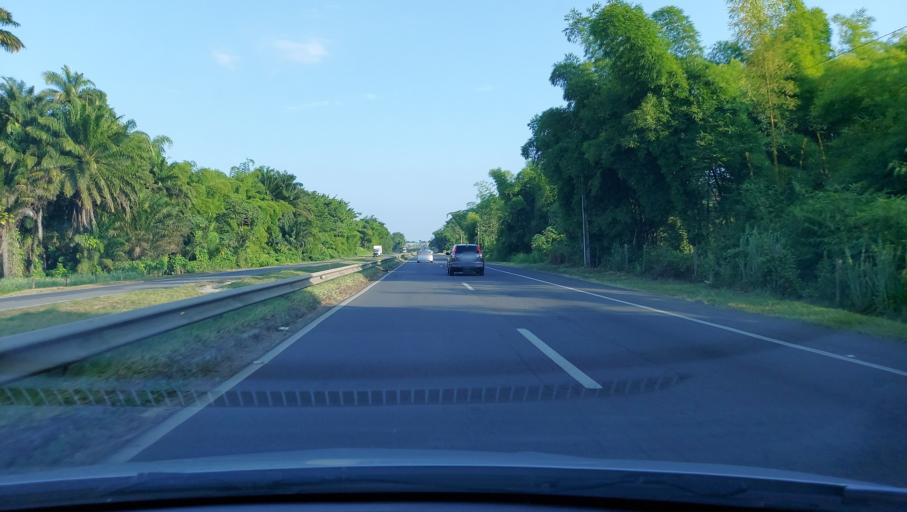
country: BR
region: Bahia
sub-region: Santo Amaro
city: Santo Amaro
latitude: -12.4412
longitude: -38.7216
